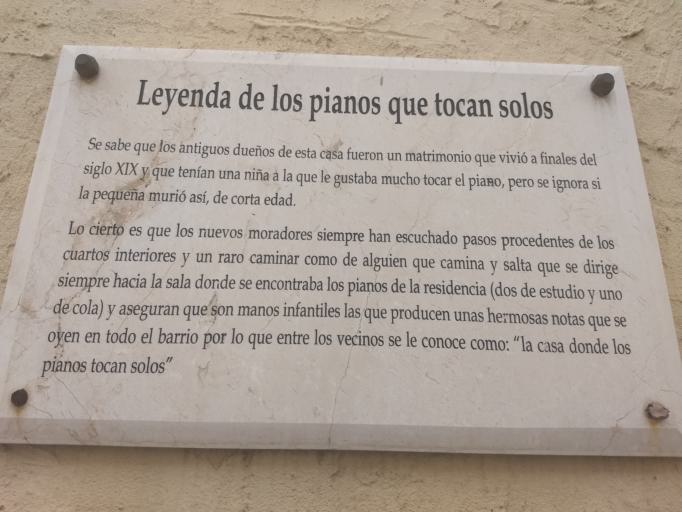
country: MX
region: Nuevo Leon
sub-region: Monterrey
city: Monterrey
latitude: 25.6650
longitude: -100.3085
